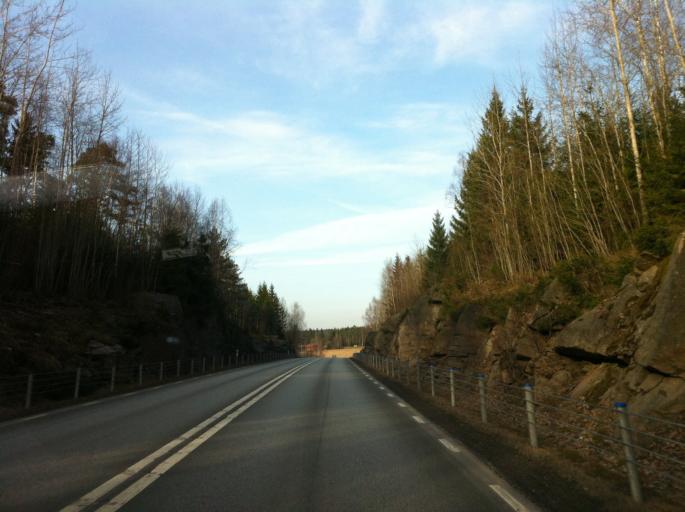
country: SE
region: Vaermland
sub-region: Storfors Kommun
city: Storfors
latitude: 59.4454
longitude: 14.2377
